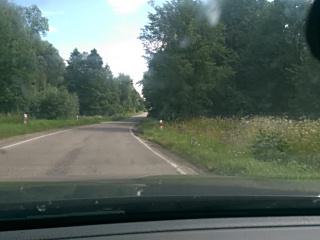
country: PL
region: Podlasie
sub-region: Powiat suwalski
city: Filipow
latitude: 54.1659
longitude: 22.5546
